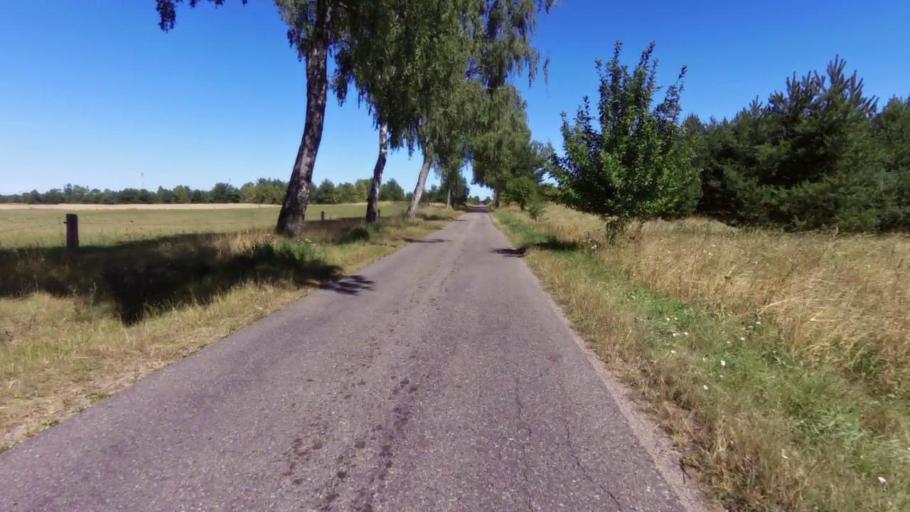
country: PL
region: West Pomeranian Voivodeship
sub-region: Powiat szczecinecki
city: Lubowo
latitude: 53.5796
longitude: 16.3756
